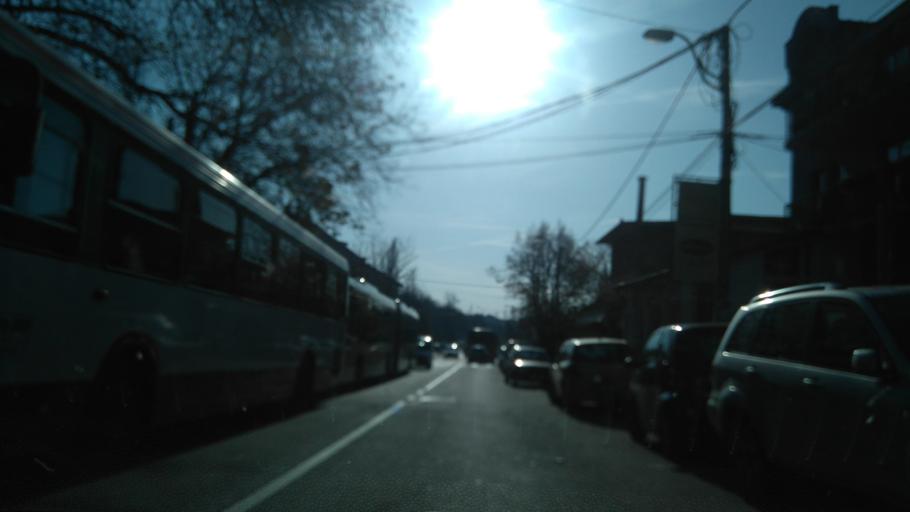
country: RS
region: Central Serbia
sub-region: Belgrade
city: Cukarica
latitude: 44.7555
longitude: 20.4043
